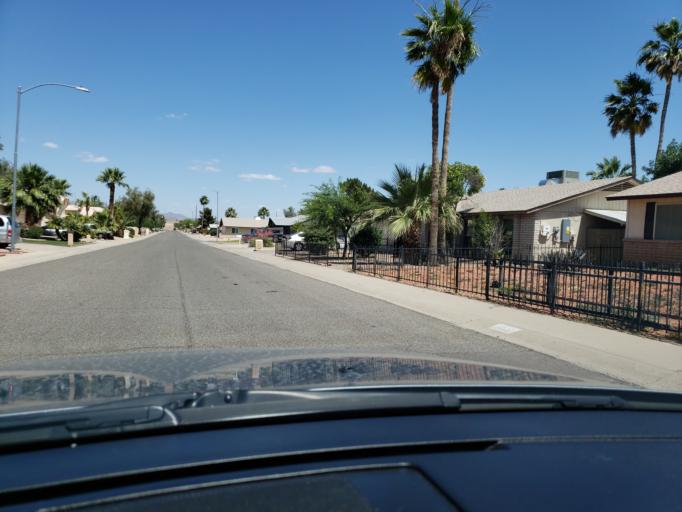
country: US
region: Arizona
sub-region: Maricopa County
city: Paradise Valley
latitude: 33.6079
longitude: -112.0174
